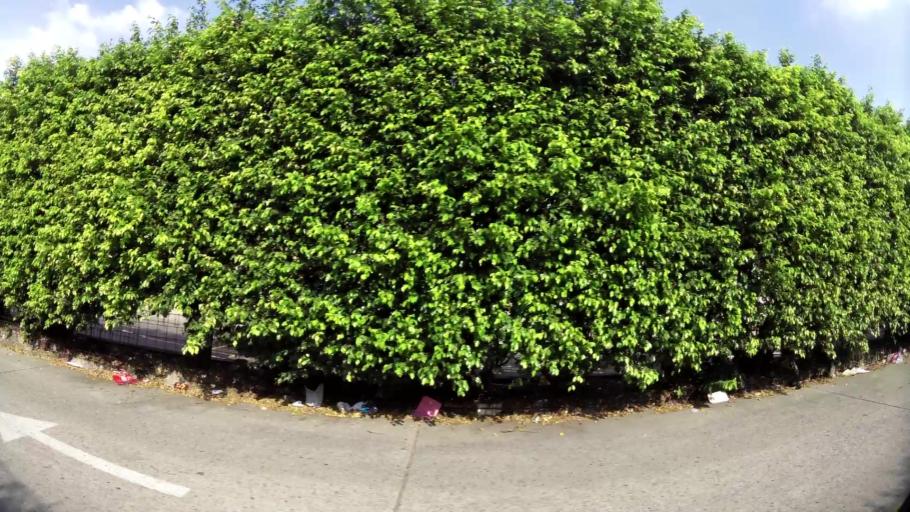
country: EC
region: Guayas
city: Guayaquil
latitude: -2.1856
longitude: -79.9032
